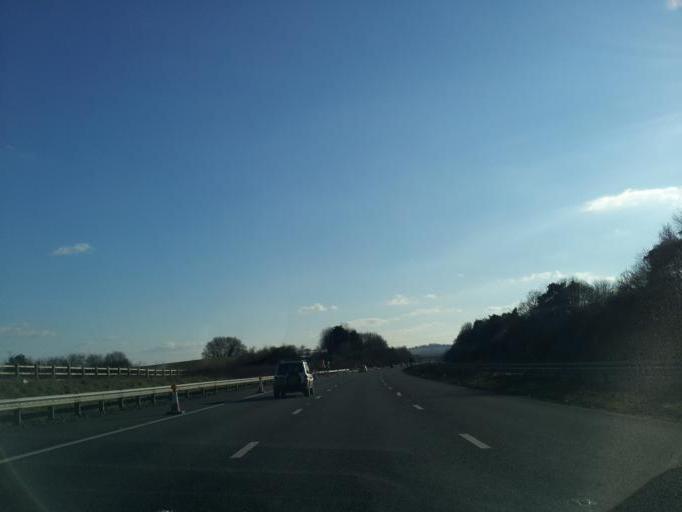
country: GB
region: England
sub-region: Devon
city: Bradninch
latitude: 50.7872
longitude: -3.4470
